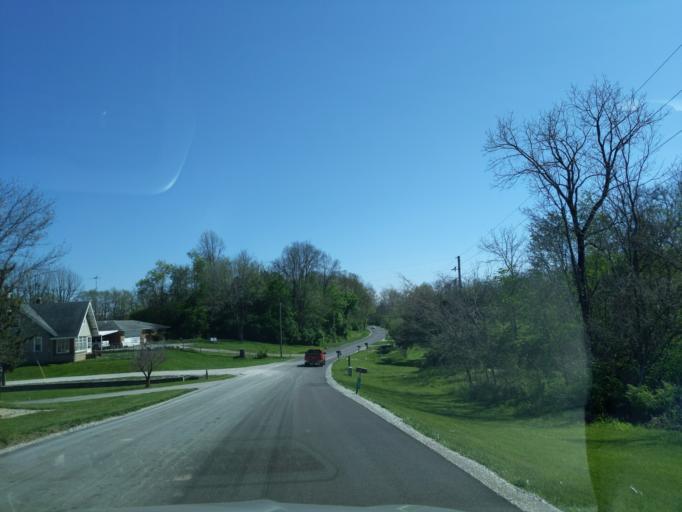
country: US
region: Indiana
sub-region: Decatur County
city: Greensburg
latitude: 39.3078
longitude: -85.4903
